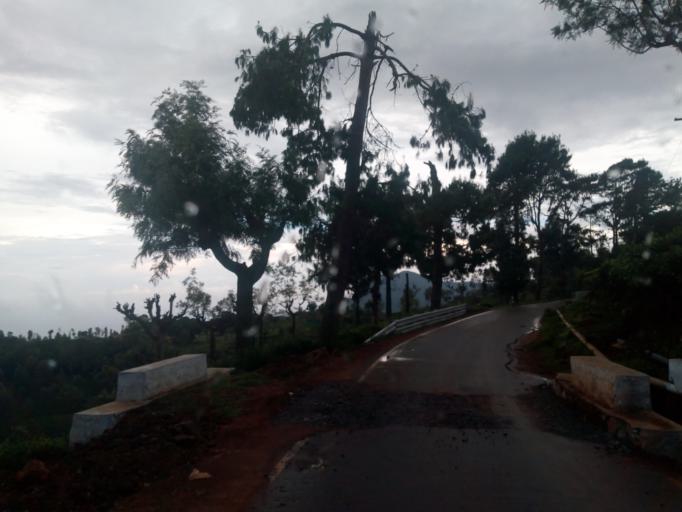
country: IN
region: Tamil Nadu
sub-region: Nilgiri
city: Wellington
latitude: 11.3559
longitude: 76.8326
